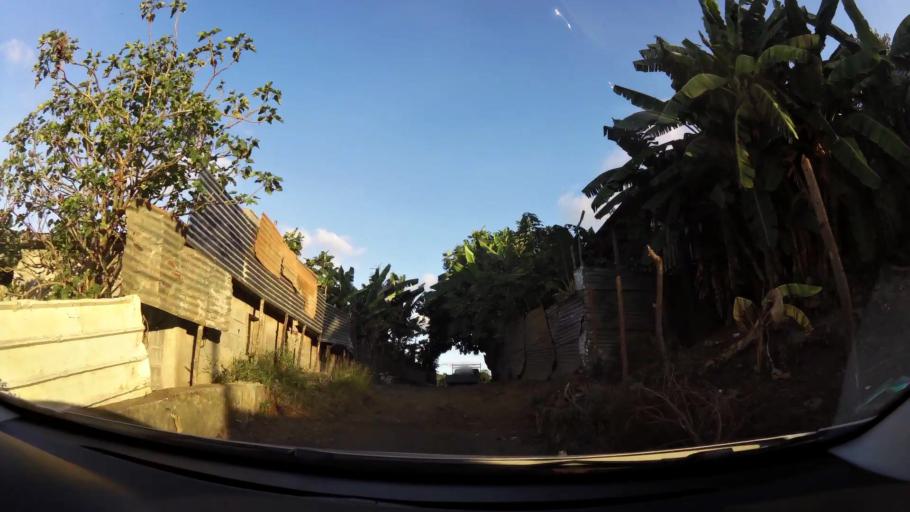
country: YT
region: Dembeni
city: Dembeni
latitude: -12.8462
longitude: 45.1883
